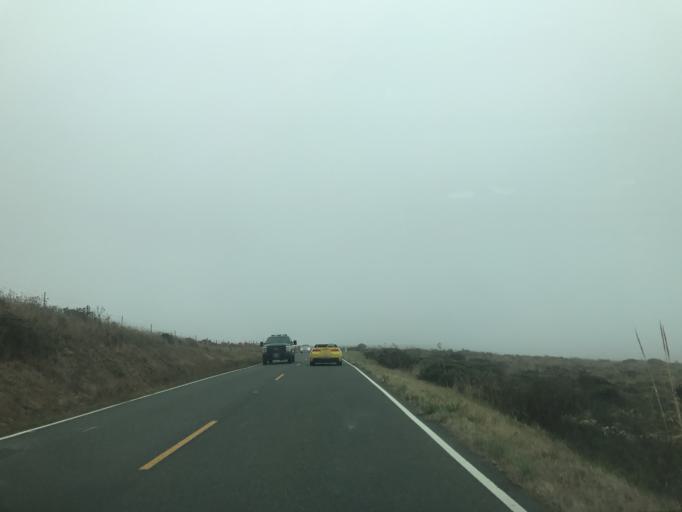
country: US
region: California
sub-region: Sonoma County
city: Monte Rio
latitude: 38.4606
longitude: -123.1442
